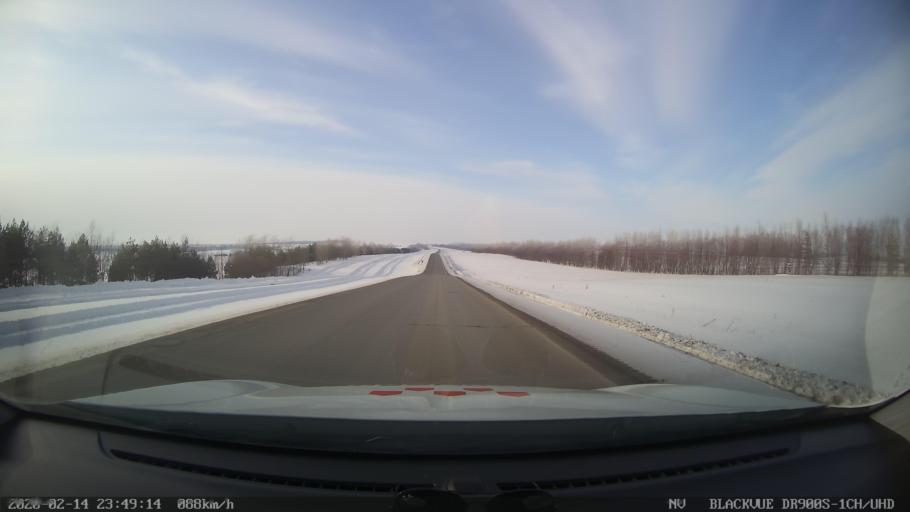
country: RU
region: Tatarstan
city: Kuybyshevskiy Zaton
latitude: 55.2522
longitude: 49.1870
